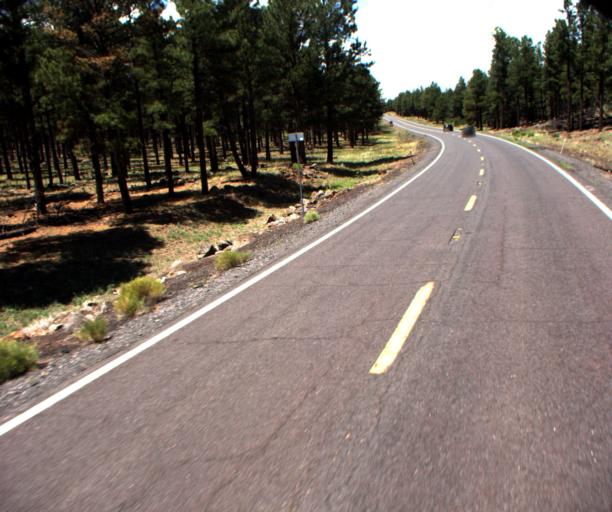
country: US
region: Arizona
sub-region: Coconino County
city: Parks
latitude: 35.4586
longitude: -111.7773
